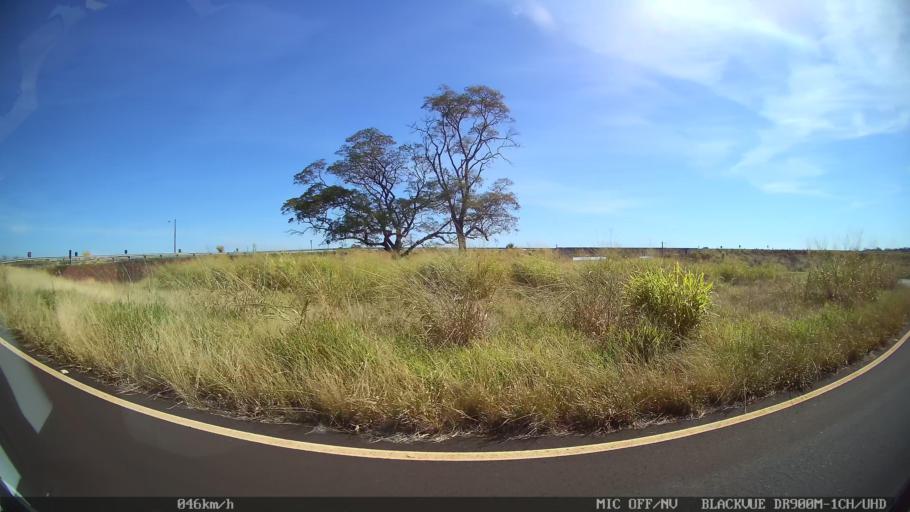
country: BR
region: Sao Paulo
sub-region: Nuporanga
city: Nuporanga
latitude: -20.5618
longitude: -47.6242
